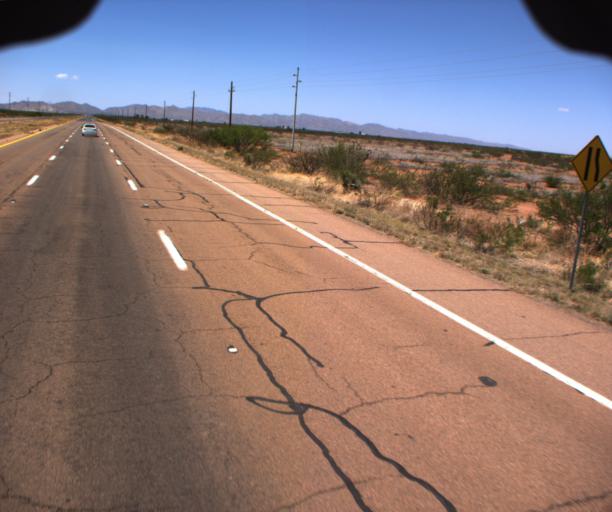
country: US
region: Arizona
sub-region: Cochise County
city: Pirtleville
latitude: 31.3574
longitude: -109.6324
